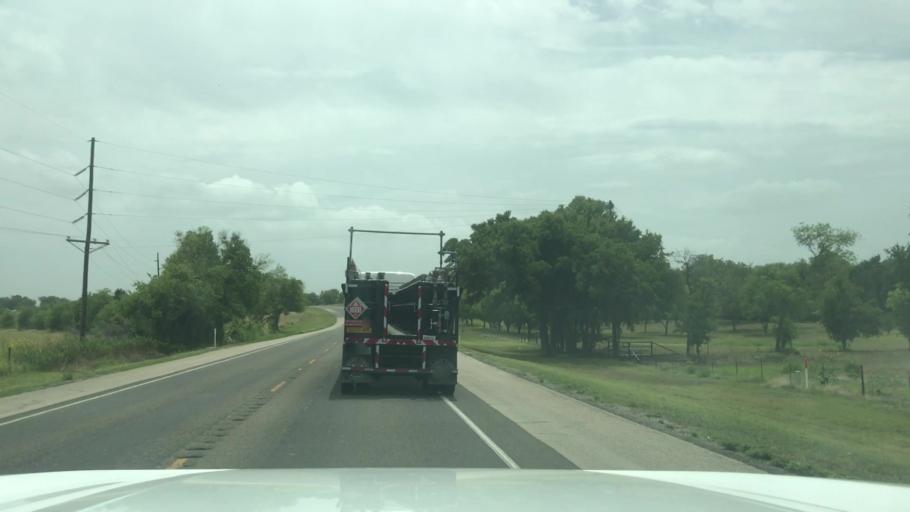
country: US
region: Texas
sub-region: Bosque County
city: Clifton
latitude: 31.7102
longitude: -97.5459
